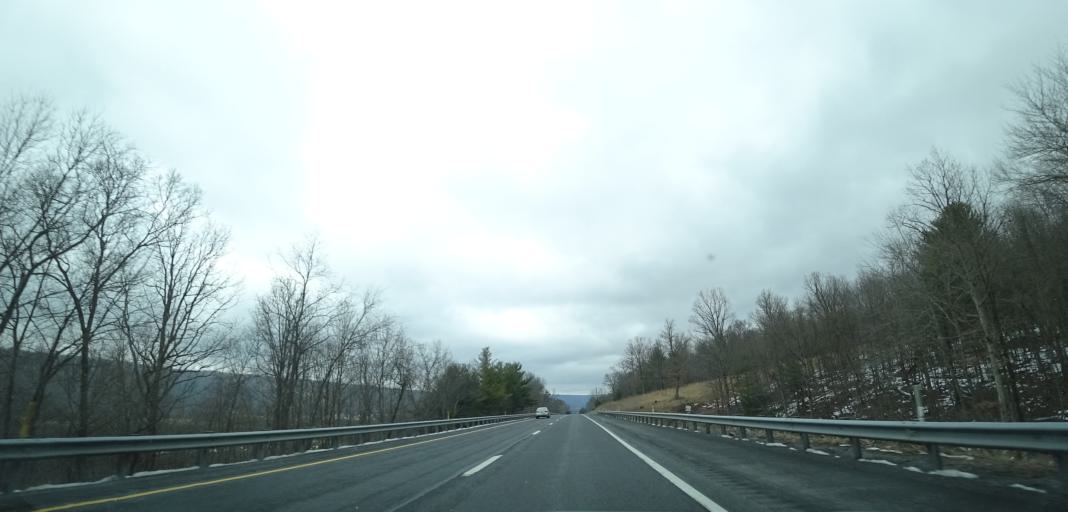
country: US
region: Pennsylvania
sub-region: Bedford County
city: Earlston
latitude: 39.9133
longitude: -78.2363
